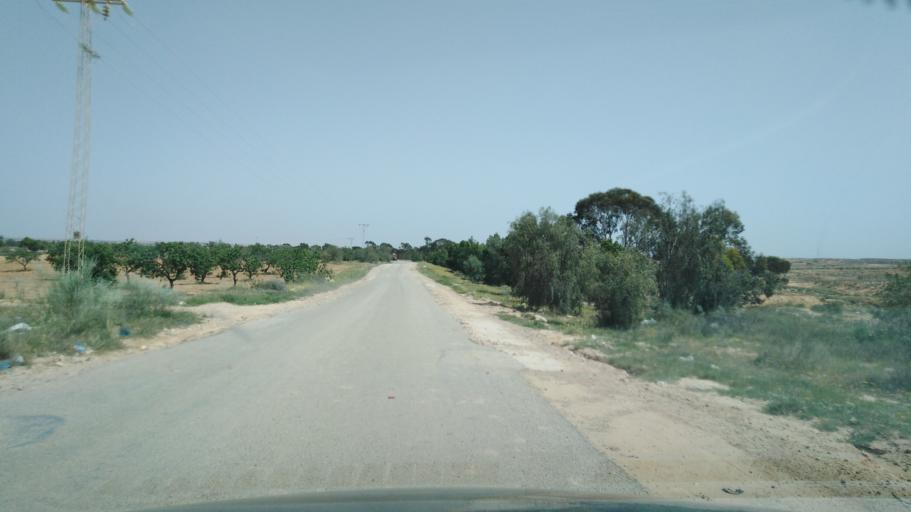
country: TN
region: Safaqis
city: Sfax
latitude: 34.7125
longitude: 10.5280
